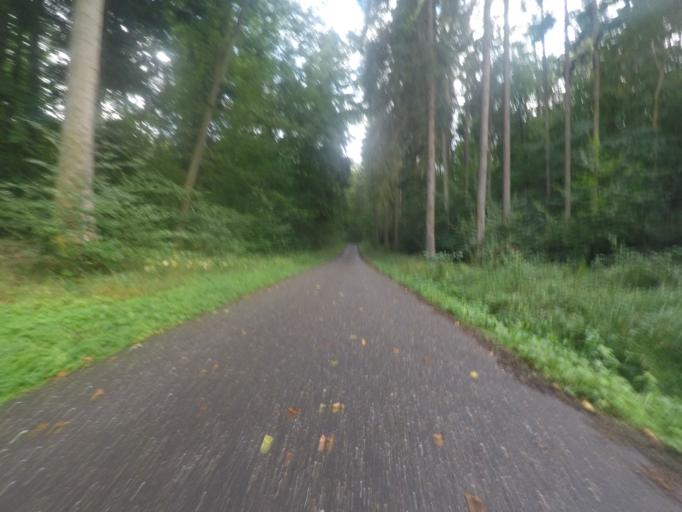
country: DE
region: Baden-Wuerttemberg
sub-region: Karlsruhe Region
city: Ettlingen
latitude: 48.8905
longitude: 8.4031
